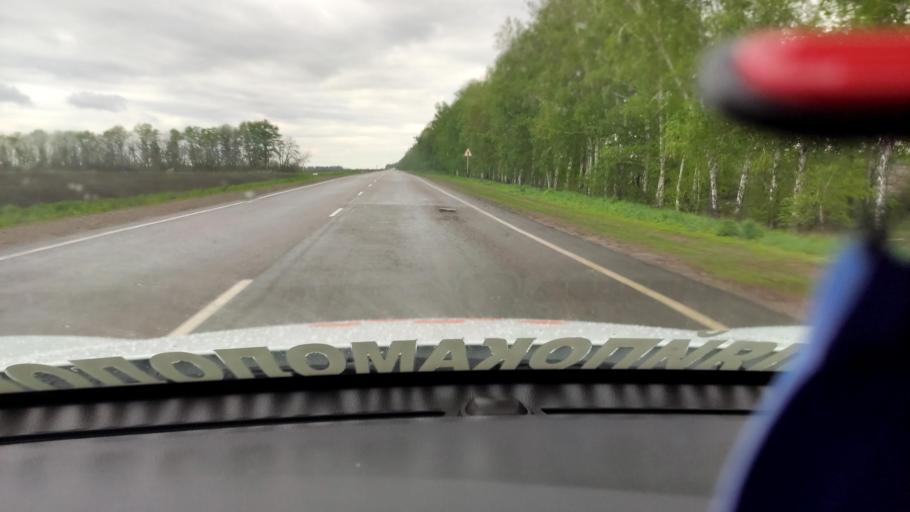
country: RU
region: Voronezj
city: Sredniy Ikorets
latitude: 51.0390
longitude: 39.6578
